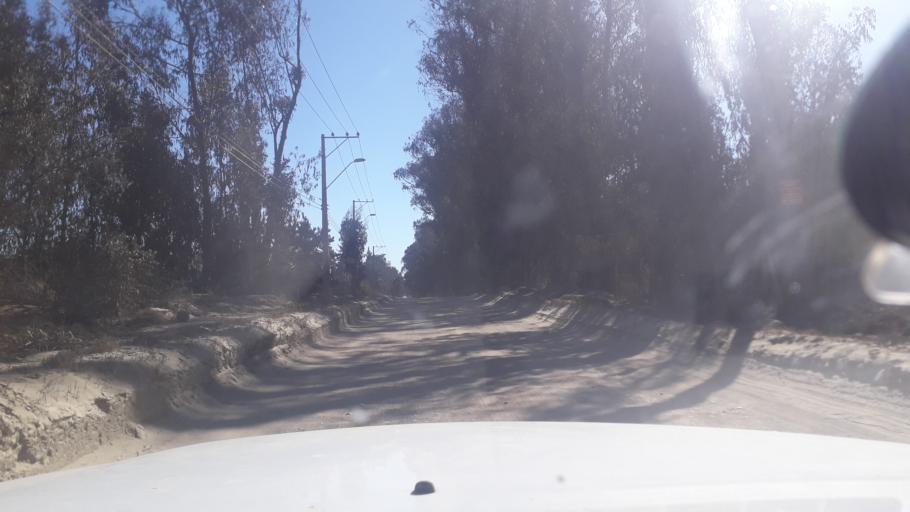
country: CL
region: Valparaiso
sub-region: Provincia de Valparaiso
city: Vina del Mar
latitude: -32.9585
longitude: -71.5138
